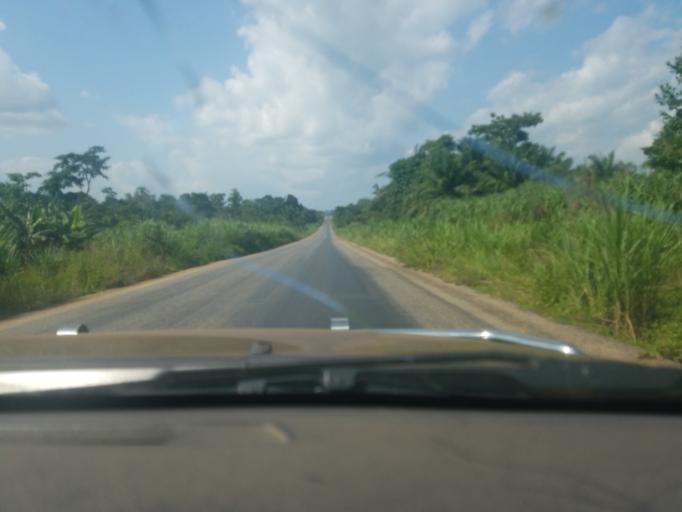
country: GH
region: Western
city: Bibiani
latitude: 6.8803
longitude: -2.4240
